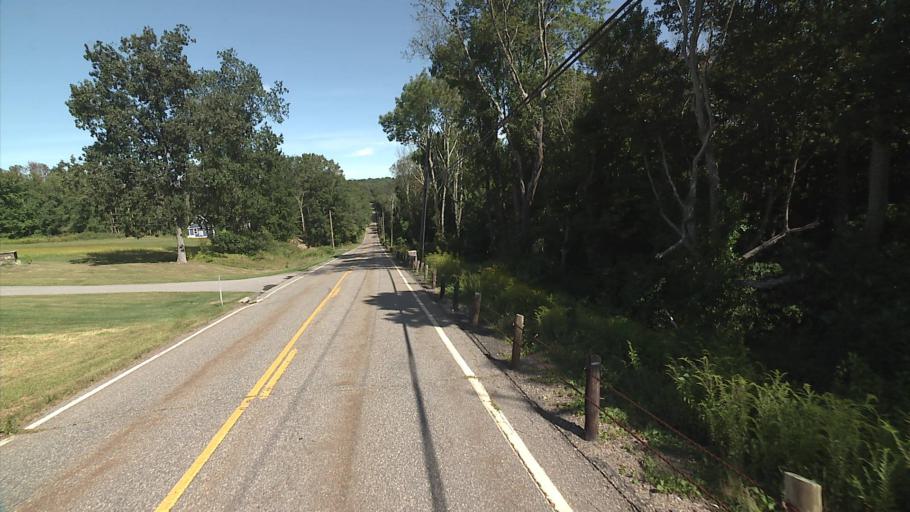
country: US
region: Connecticut
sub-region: Litchfield County
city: Northwest Harwinton
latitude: 41.7392
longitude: -73.0771
